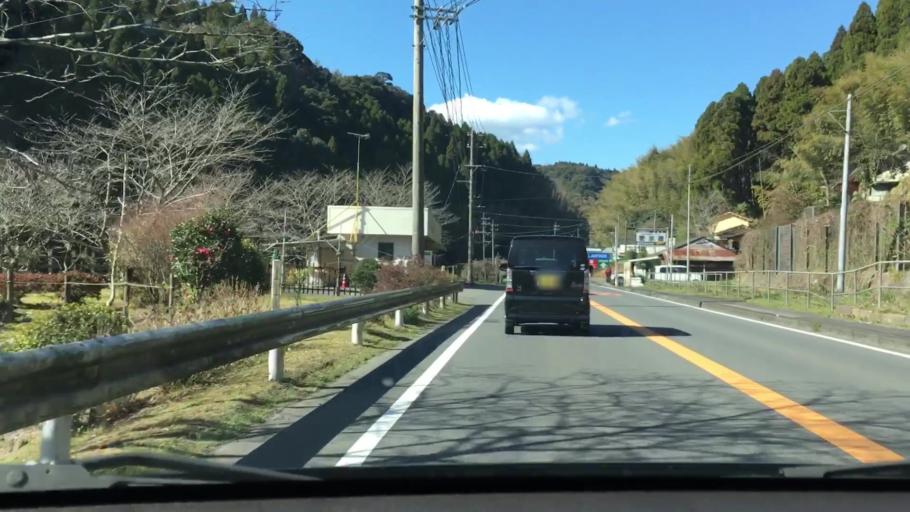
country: JP
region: Kagoshima
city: Ijuin
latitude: 31.6517
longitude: 130.5016
